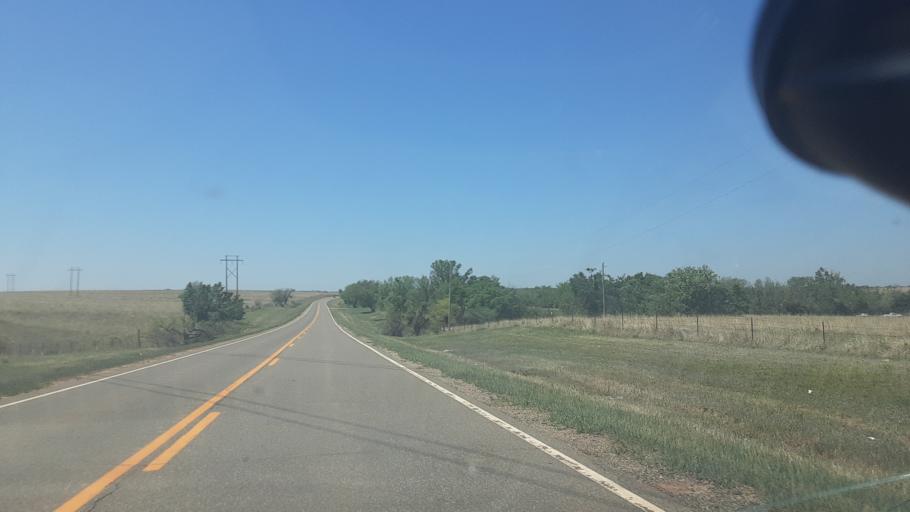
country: US
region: Oklahoma
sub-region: Noble County
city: Perry
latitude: 36.1136
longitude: -97.3772
